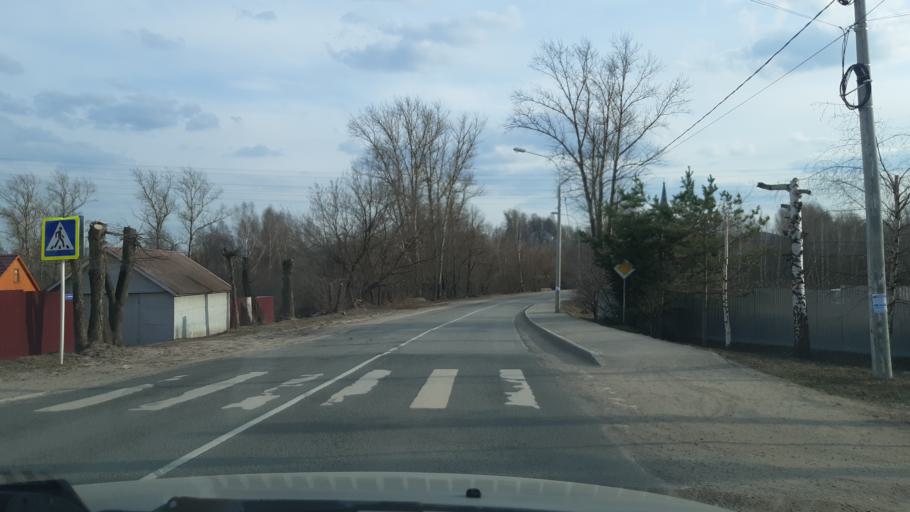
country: RU
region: Vladimir
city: Nikologory
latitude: 56.1443
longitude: 41.9936
